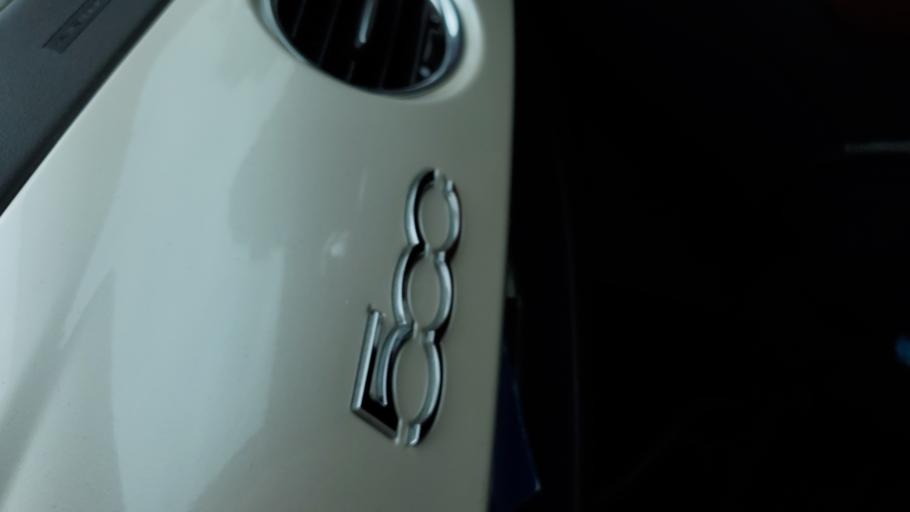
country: FR
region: Ile-de-France
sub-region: Departement de Seine-et-Marne
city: Pommeuse
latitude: 48.8331
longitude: 3.0036
